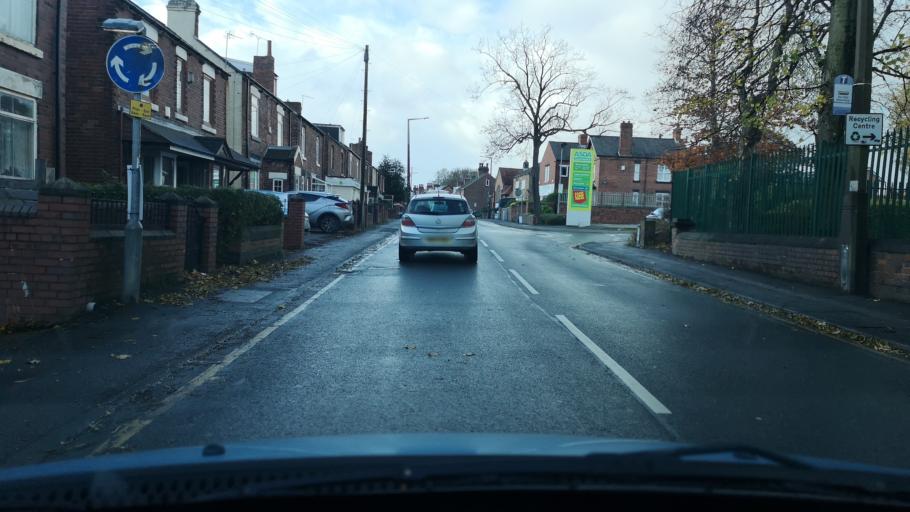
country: GB
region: England
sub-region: Barnsley
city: Royston
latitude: 53.6001
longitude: -1.4499
